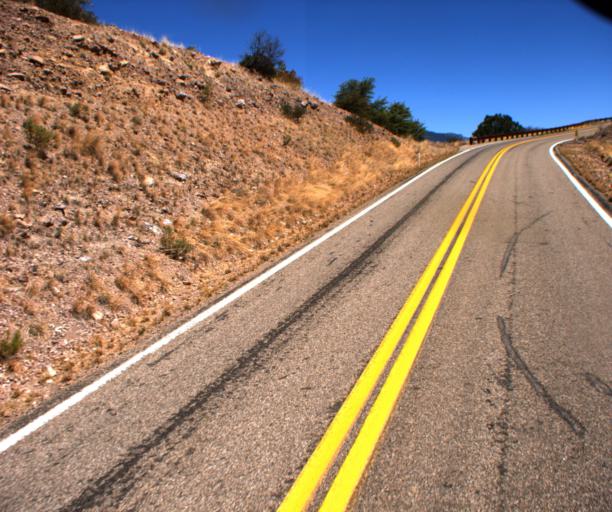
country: US
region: Arizona
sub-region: Cochise County
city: Sierra Vista
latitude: 31.4828
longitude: -110.4832
